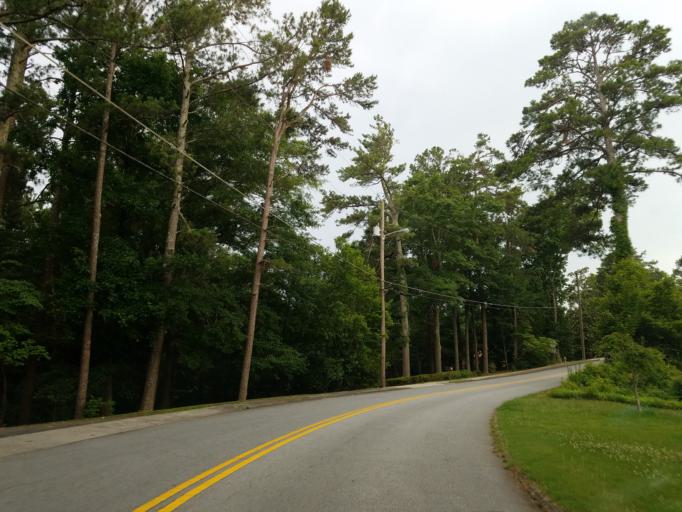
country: US
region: Georgia
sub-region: Cobb County
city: Marietta
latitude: 33.9334
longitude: -84.5668
